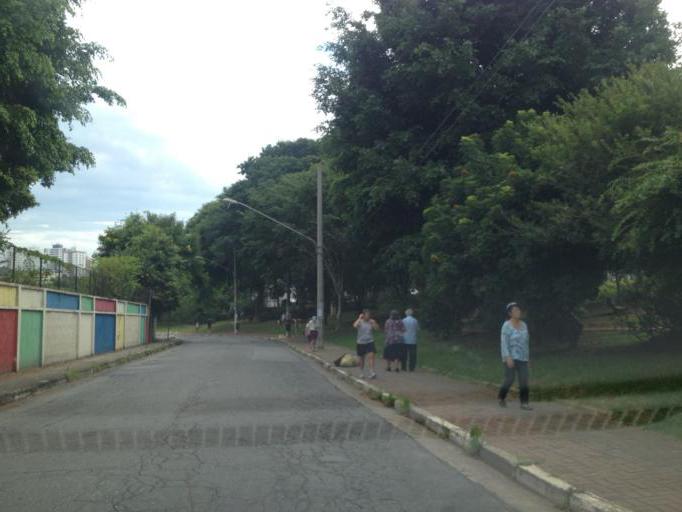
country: BR
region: Sao Paulo
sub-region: Osasco
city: Osasco
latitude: -23.5770
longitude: -46.7308
